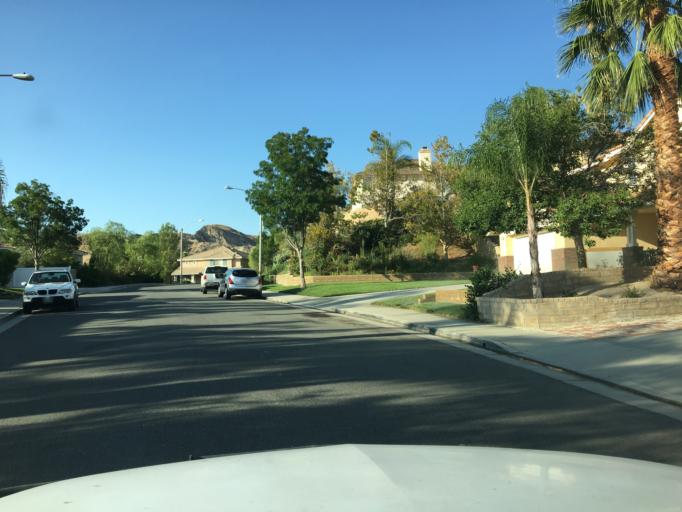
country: US
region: California
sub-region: Los Angeles County
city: Castaic
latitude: 34.5106
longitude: -118.6374
